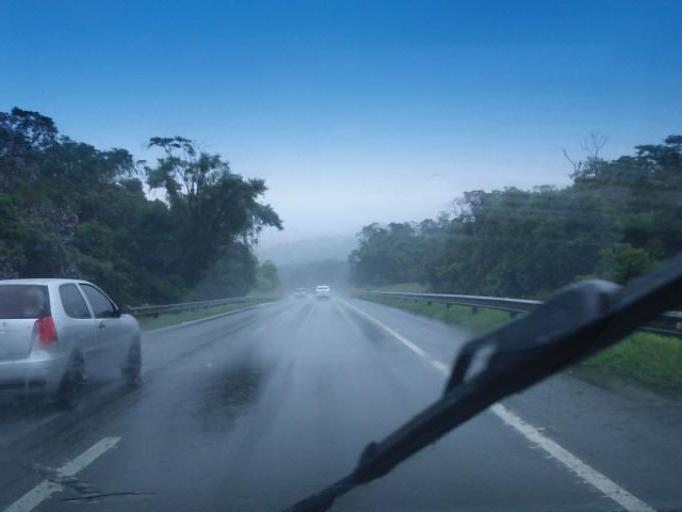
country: BR
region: Parana
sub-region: Guaratuba
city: Guaratuba
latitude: -25.9445
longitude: -48.9069
